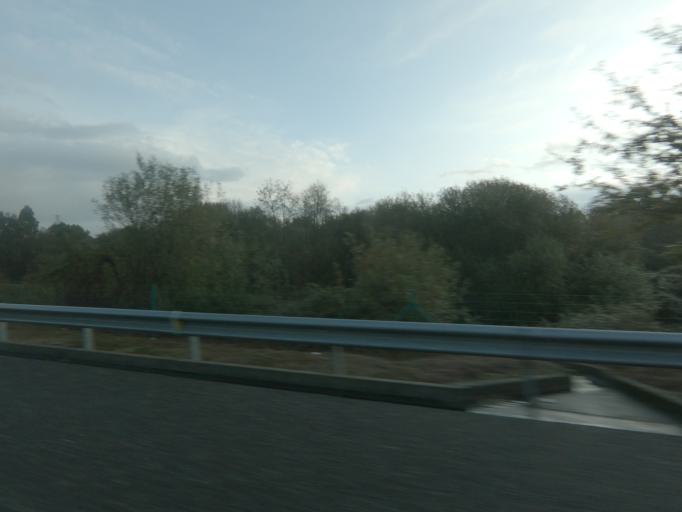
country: ES
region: Galicia
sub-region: Provincia de Pontevedra
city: Tui
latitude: 42.0926
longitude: -8.6430
